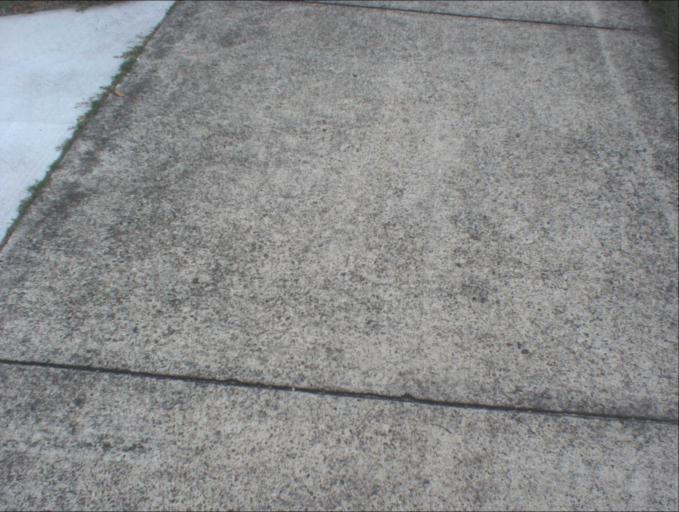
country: AU
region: Queensland
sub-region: Logan
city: Park Ridge South
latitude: -27.6815
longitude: 153.0575
